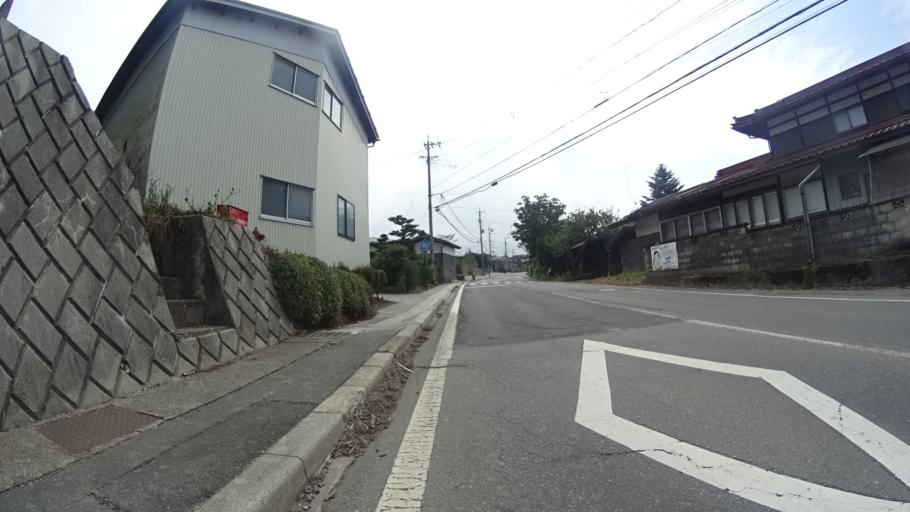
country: JP
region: Nagano
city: Chino
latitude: 35.9565
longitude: 138.2327
